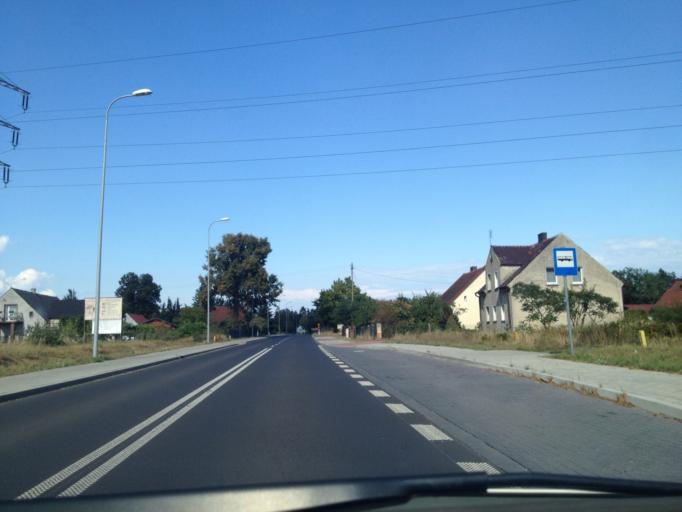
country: PL
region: Lubusz
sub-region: Powiat zaganski
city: Ilowa
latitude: 51.5123
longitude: 15.2094
